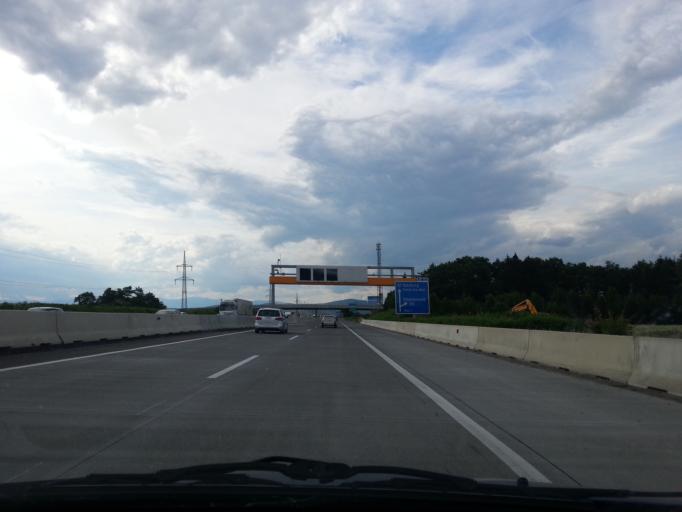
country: AT
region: Styria
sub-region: Politischer Bezirk Graz-Umgebung
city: Zettling
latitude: 46.9669
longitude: 15.4339
